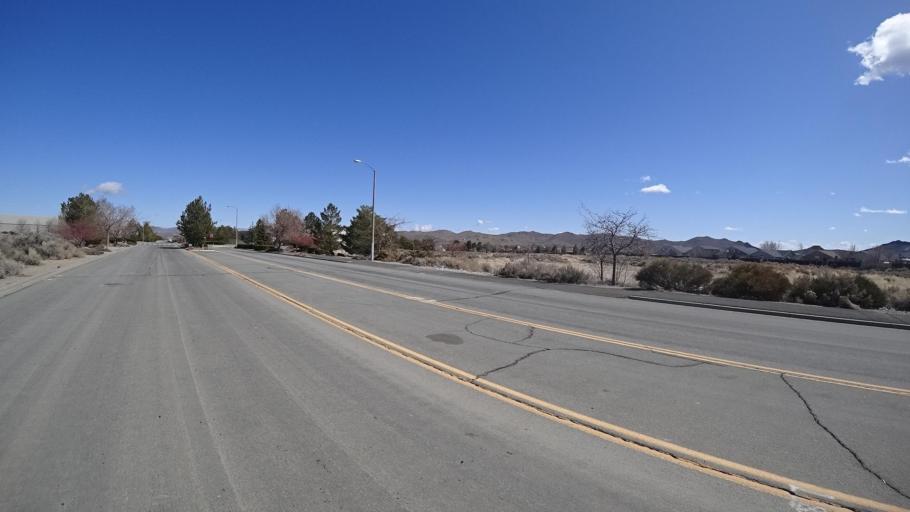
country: US
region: Nevada
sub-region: Washoe County
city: Lemmon Valley
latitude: 39.6434
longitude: -119.8654
